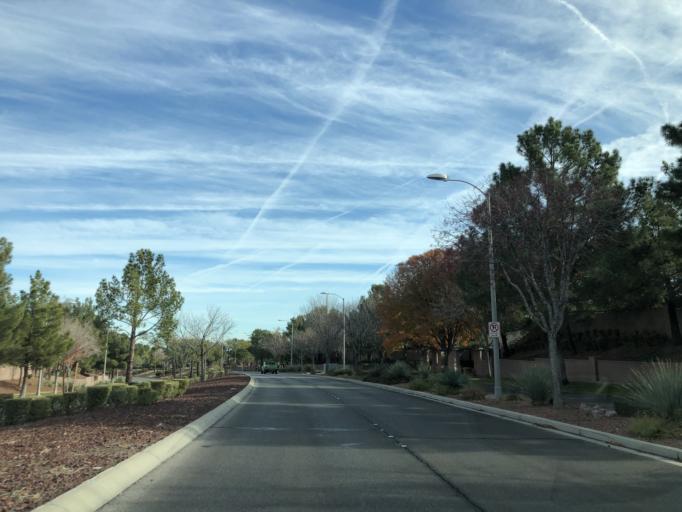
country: US
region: Nevada
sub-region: Clark County
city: Whitney
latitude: 36.0179
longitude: -115.0716
